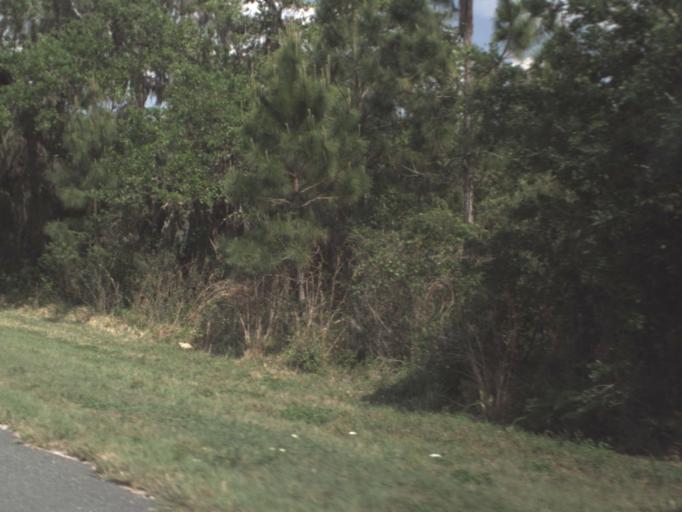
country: US
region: Florida
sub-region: Lake County
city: Howie In The Hills
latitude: 28.6549
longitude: -81.7915
